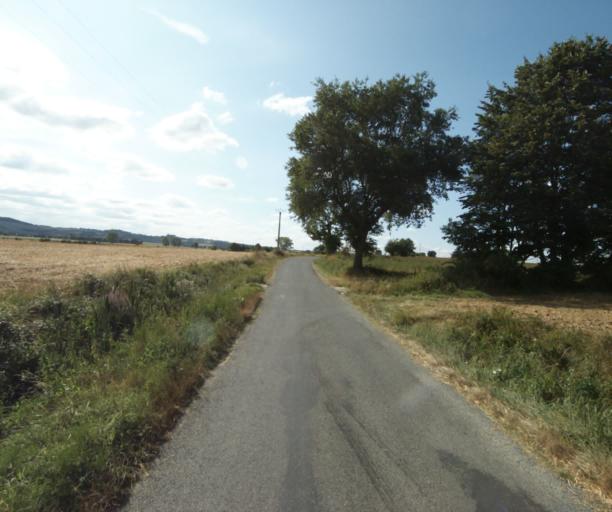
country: FR
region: Midi-Pyrenees
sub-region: Departement du Tarn
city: Puylaurens
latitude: 43.5286
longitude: 1.9769
